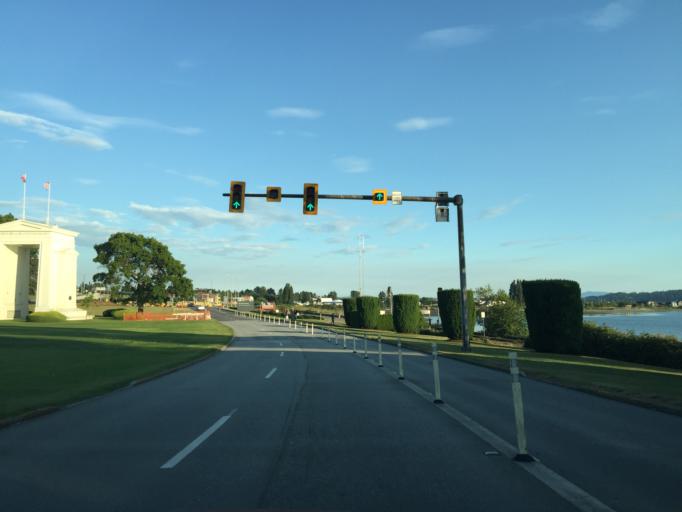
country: US
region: Washington
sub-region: Whatcom County
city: Blaine
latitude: 49.0029
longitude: -122.7576
